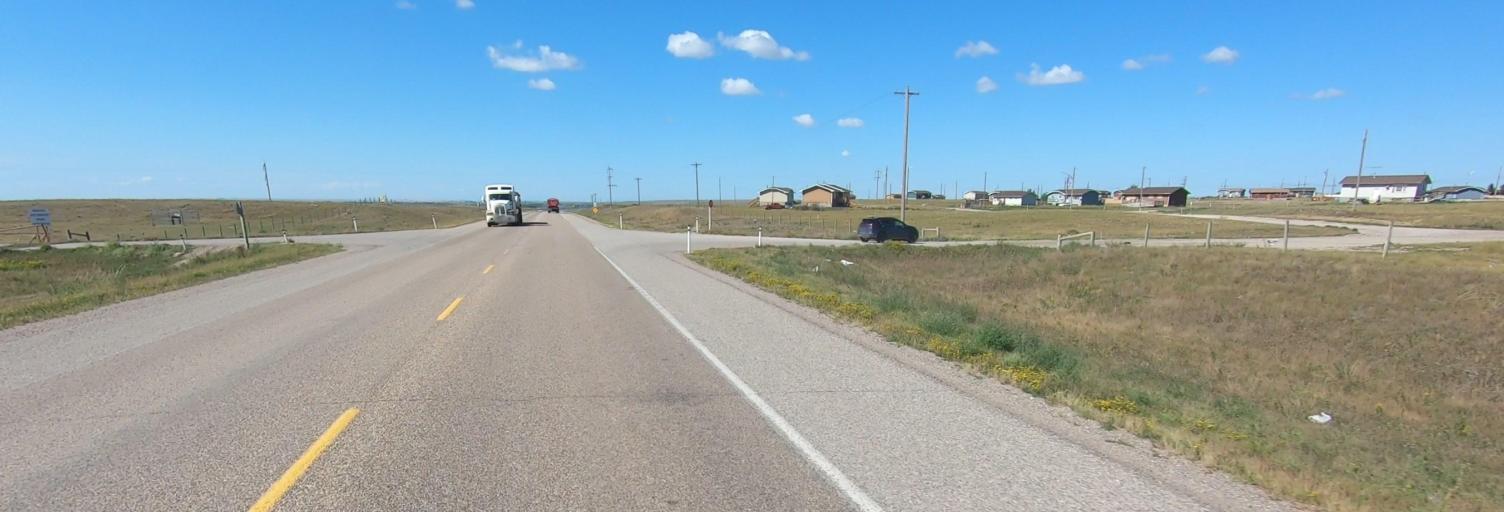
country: CA
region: Alberta
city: Strathmore
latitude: 50.8483
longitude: -113.0740
